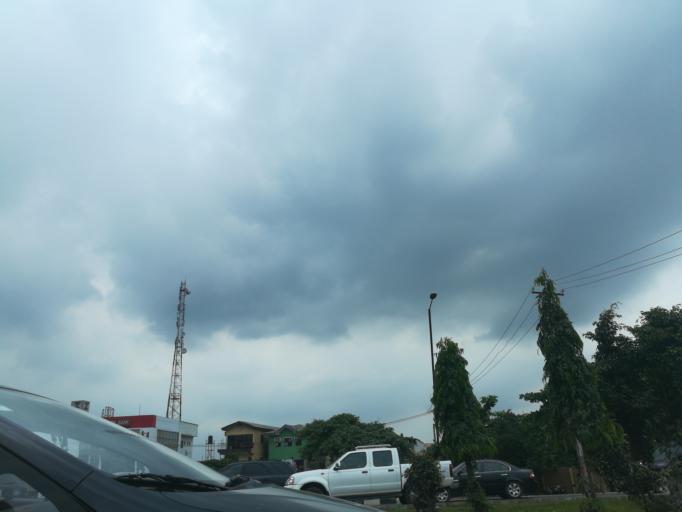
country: NG
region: Lagos
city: Ojota
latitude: 6.5992
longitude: 3.3785
